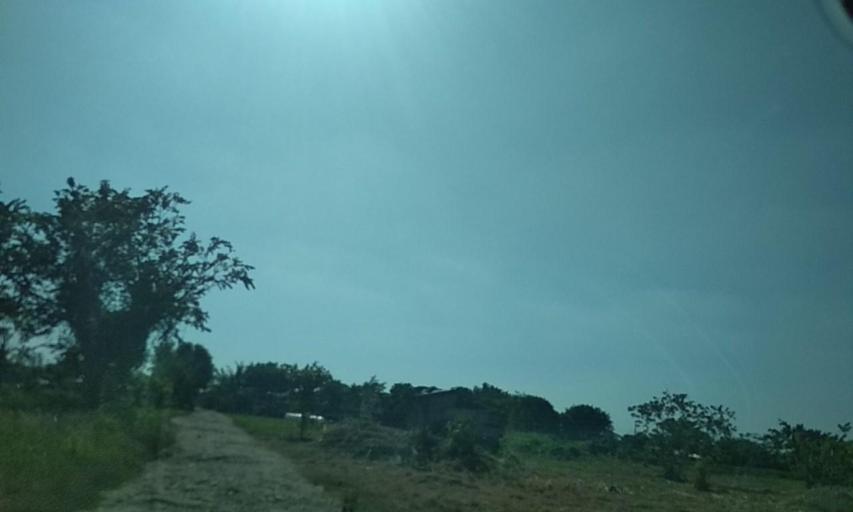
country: MX
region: Veracruz
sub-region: Martinez de la Torre
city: La Union Paso Largo
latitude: 20.1436
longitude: -96.9955
